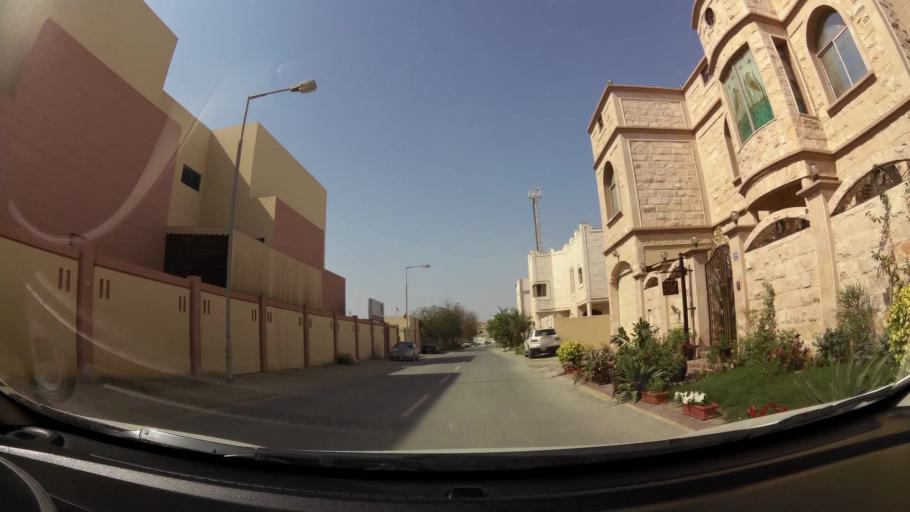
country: BH
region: Manama
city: Jidd Hafs
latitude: 26.2063
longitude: 50.4595
